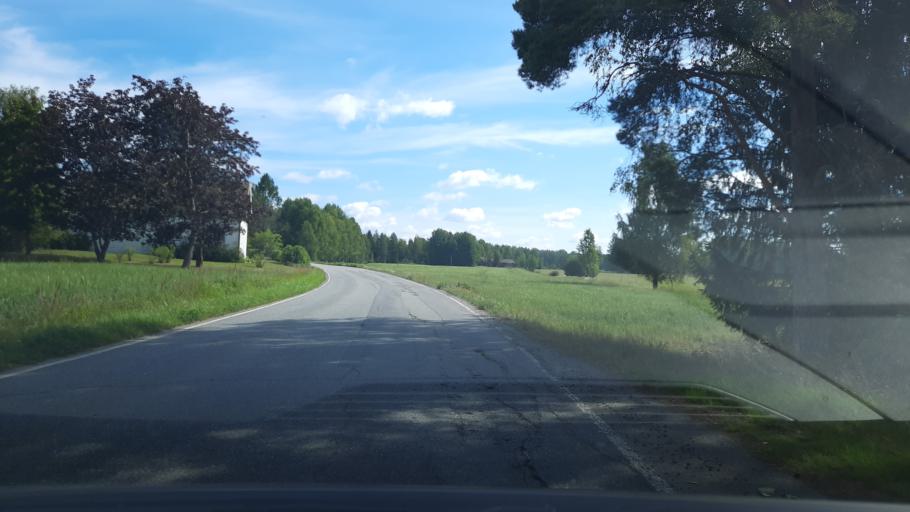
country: FI
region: Pirkanmaa
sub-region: Lounais-Pirkanmaa
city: Punkalaidun
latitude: 61.1901
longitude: 23.3006
